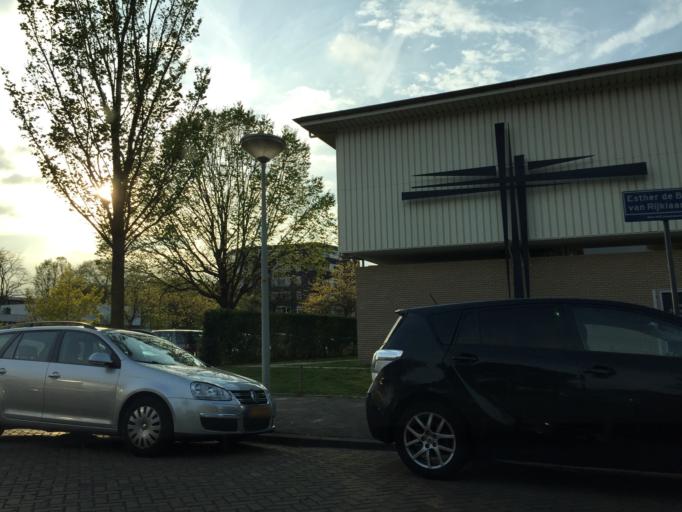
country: NL
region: South Holland
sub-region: Gemeente Den Haag
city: The Hague
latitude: 52.1047
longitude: 4.3258
